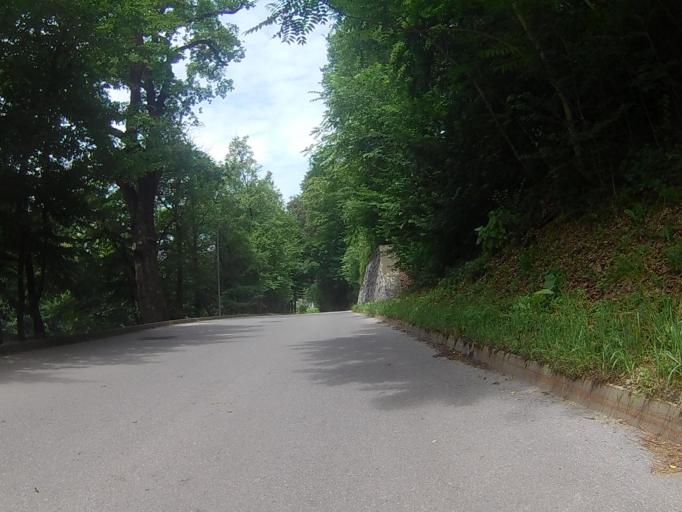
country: SI
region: Maribor
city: Maribor
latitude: 46.5710
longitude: 15.6478
